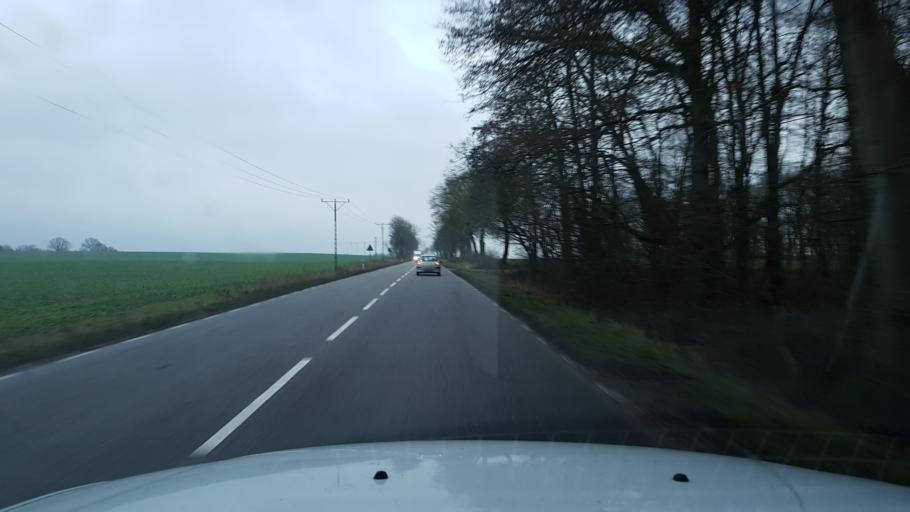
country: PL
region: West Pomeranian Voivodeship
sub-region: Powiat gryficki
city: Gryfice
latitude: 53.8559
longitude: 15.2269
